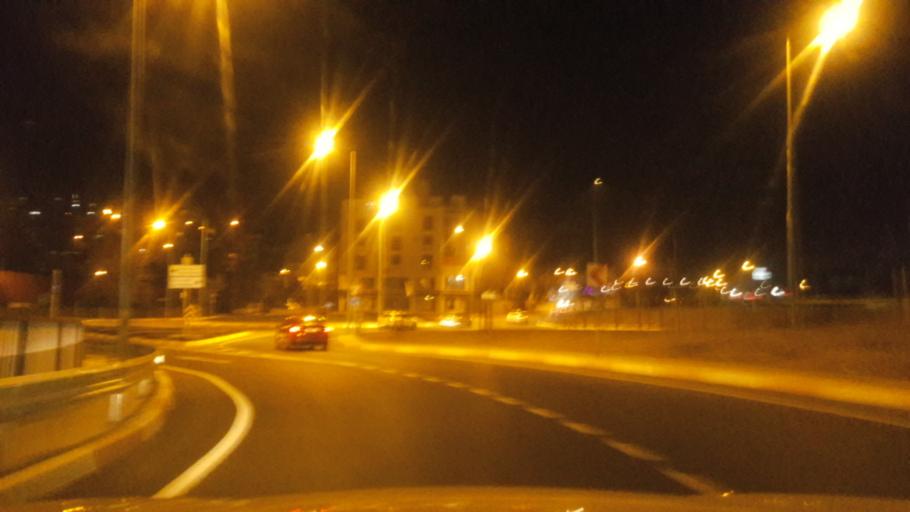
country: TR
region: Kocaeli
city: Tavsanli
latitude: 40.7899
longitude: 29.5305
